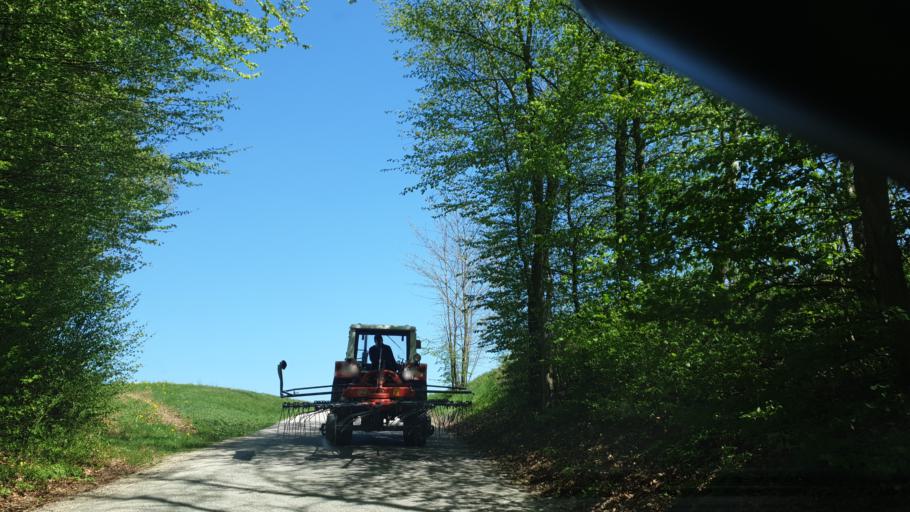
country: AT
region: Upper Austria
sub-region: Politischer Bezirk Vocklabruck
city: Gampern
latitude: 47.9979
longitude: 13.5591
